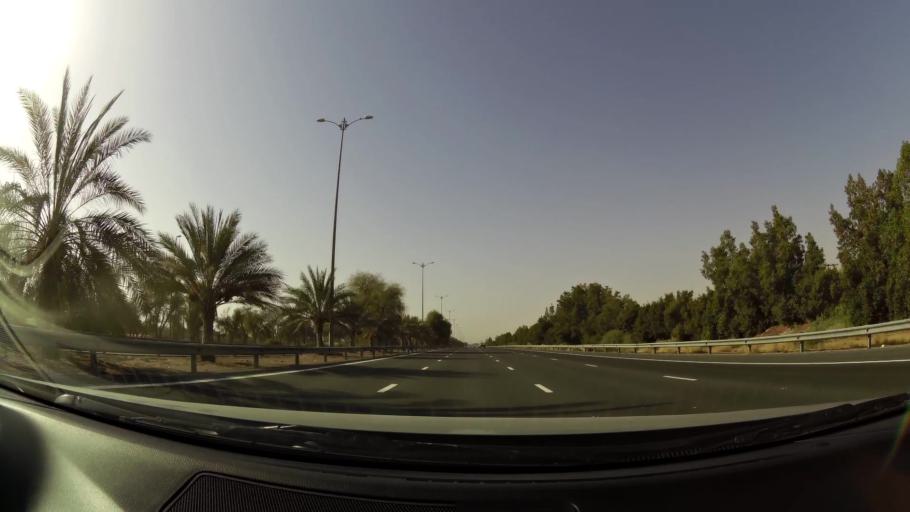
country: OM
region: Al Buraimi
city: Al Buraymi
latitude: 24.6105
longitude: 55.7294
